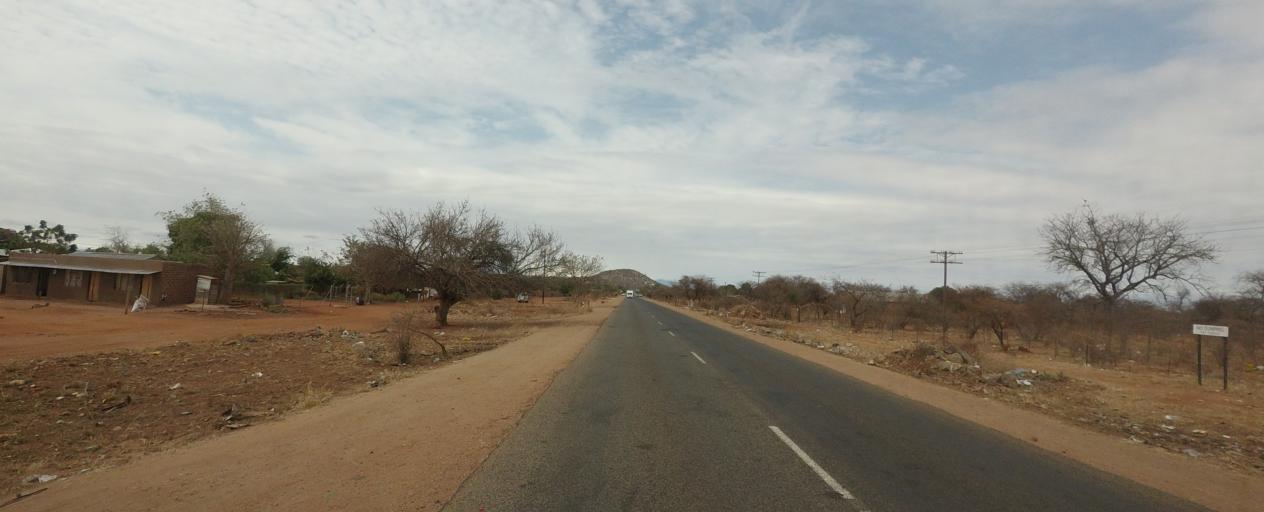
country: BW
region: Central
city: Mathathane
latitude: -22.6704
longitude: 29.1110
